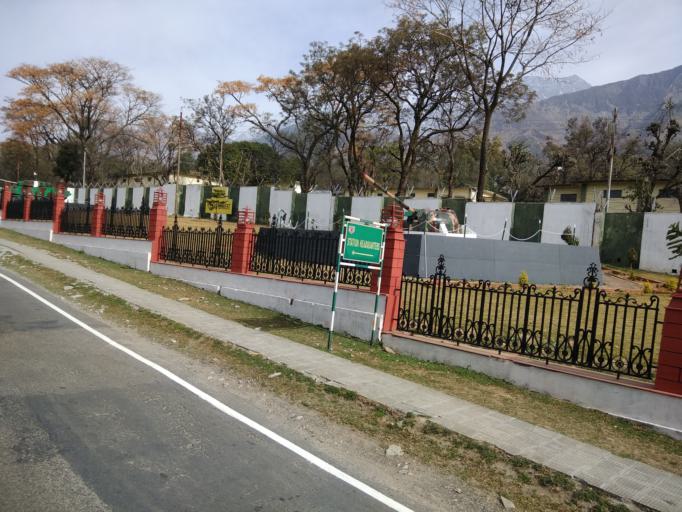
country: IN
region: Himachal Pradesh
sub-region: Kangra
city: Dharmsala
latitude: 32.1768
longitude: 76.3806
